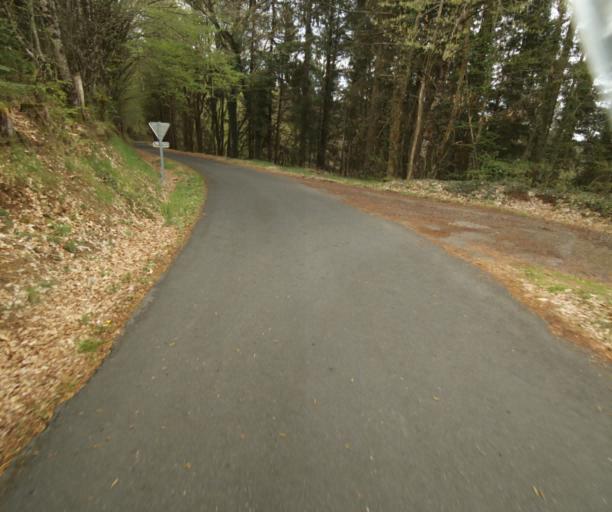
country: FR
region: Limousin
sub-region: Departement de la Correze
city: Naves
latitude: 45.3049
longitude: 1.8077
